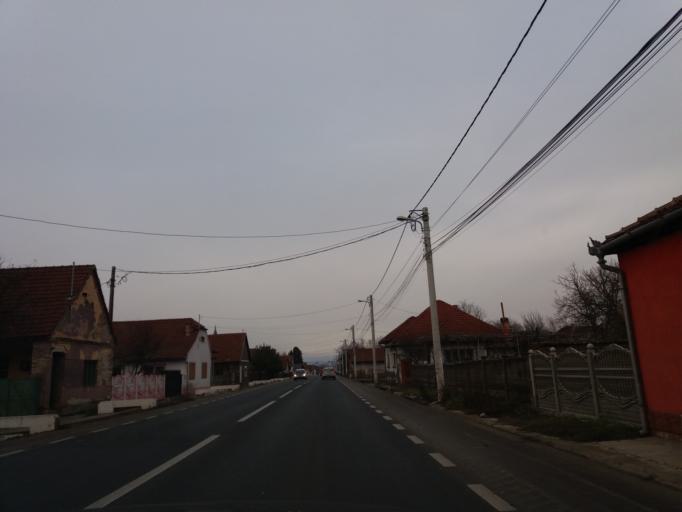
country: RO
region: Hunedoara
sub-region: Comuna Bacia
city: Bacia
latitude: 45.7808
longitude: 23.0010
